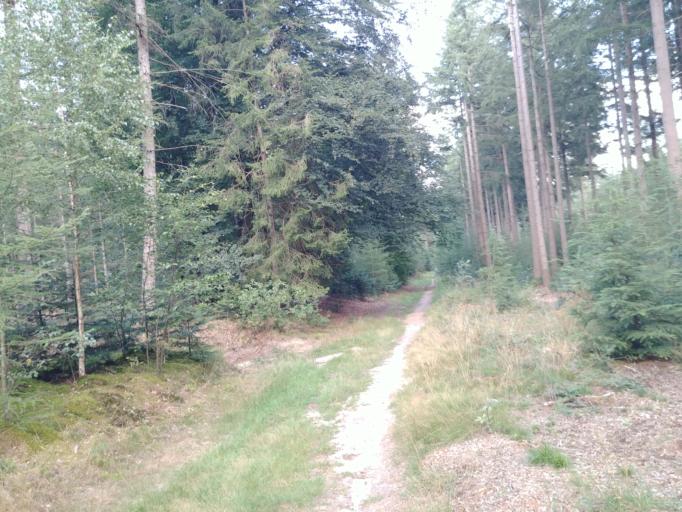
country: NL
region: Utrecht
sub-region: Gemeente Utrechtse Heuvelrug
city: Maarn
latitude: 52.0507
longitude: 5.3611
